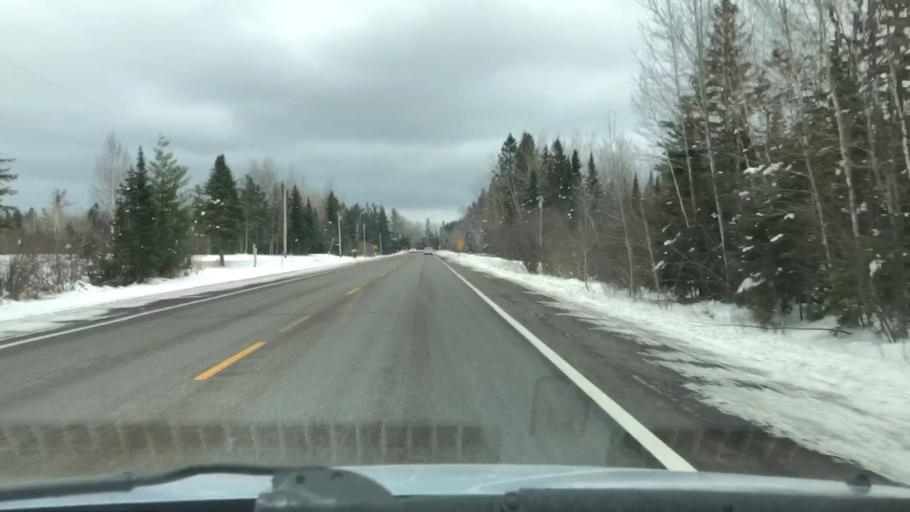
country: US
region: Minnesota
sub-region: Carlton County
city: Esko
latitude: 46.6885
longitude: -92.3648
